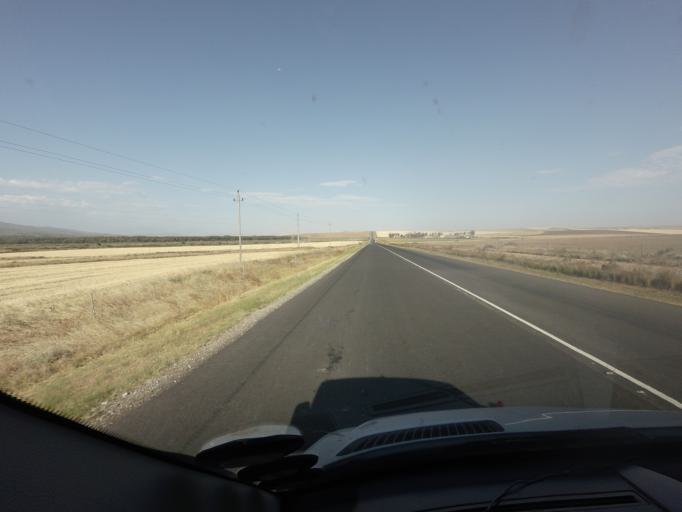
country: ZA
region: Western Cape
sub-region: Cape Winelands District Municipality
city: Ashton
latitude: -34.1533
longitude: 19.9243
